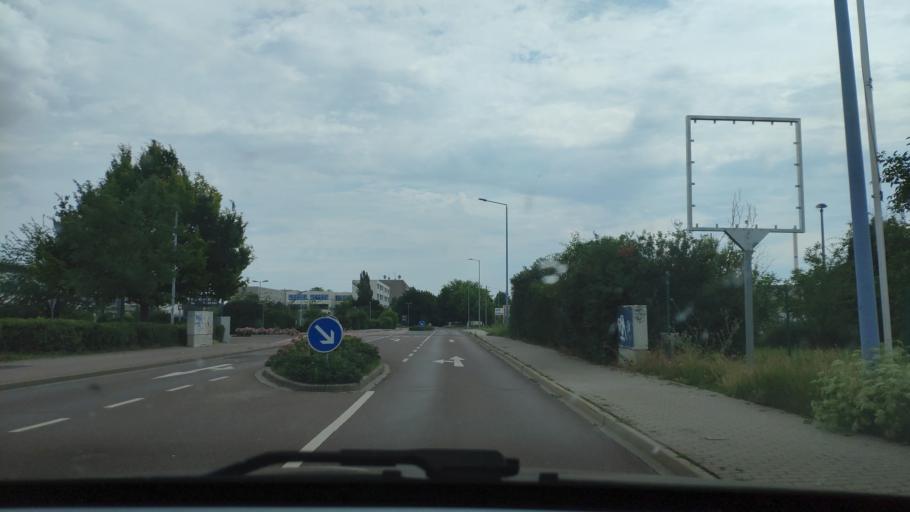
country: DE
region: Saxony-Anhalt
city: Bernburg
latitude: 51.7809
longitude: 11.7518
